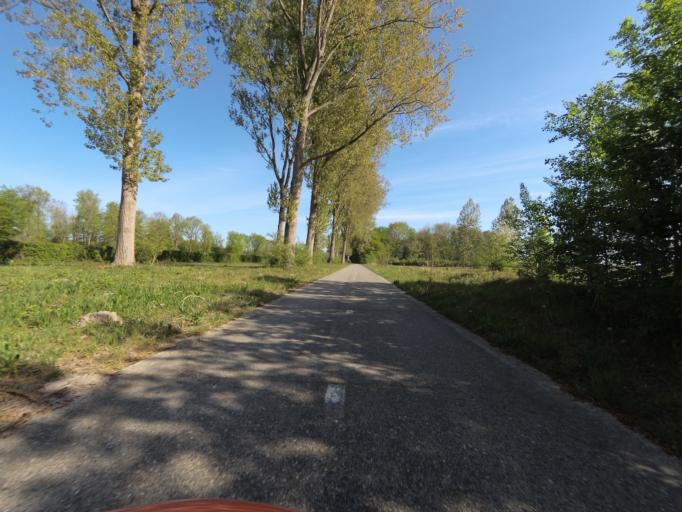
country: NL
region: Gelderland
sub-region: Gemeente Elburg
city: Elburg
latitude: 52.5049
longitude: 5.8510
